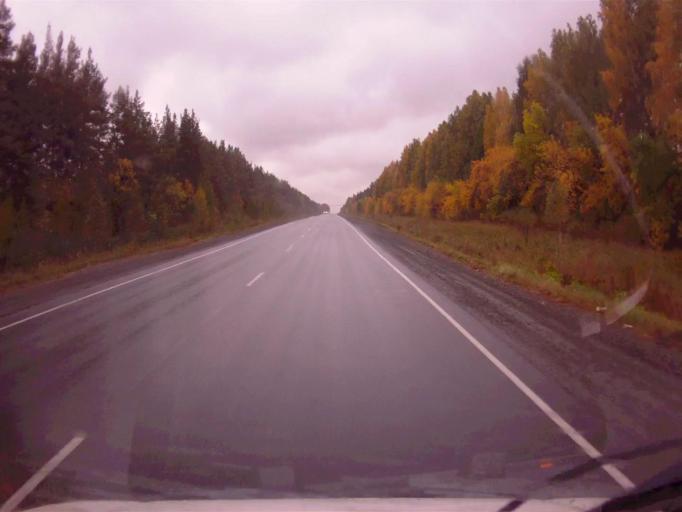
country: RU
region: Chelyabinsk
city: Roshchino
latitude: 55.3763
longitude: 61.1495
